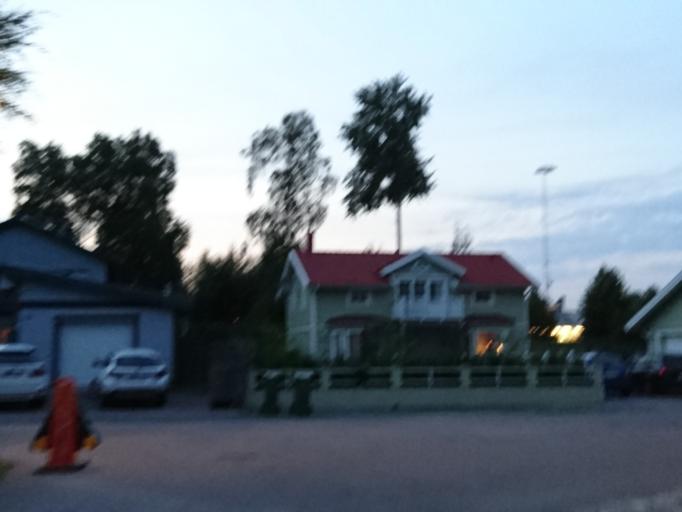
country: SE
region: Stockholm
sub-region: Huddinge Kommun
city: Segeltorp
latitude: 59.2830
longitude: 17.9414
